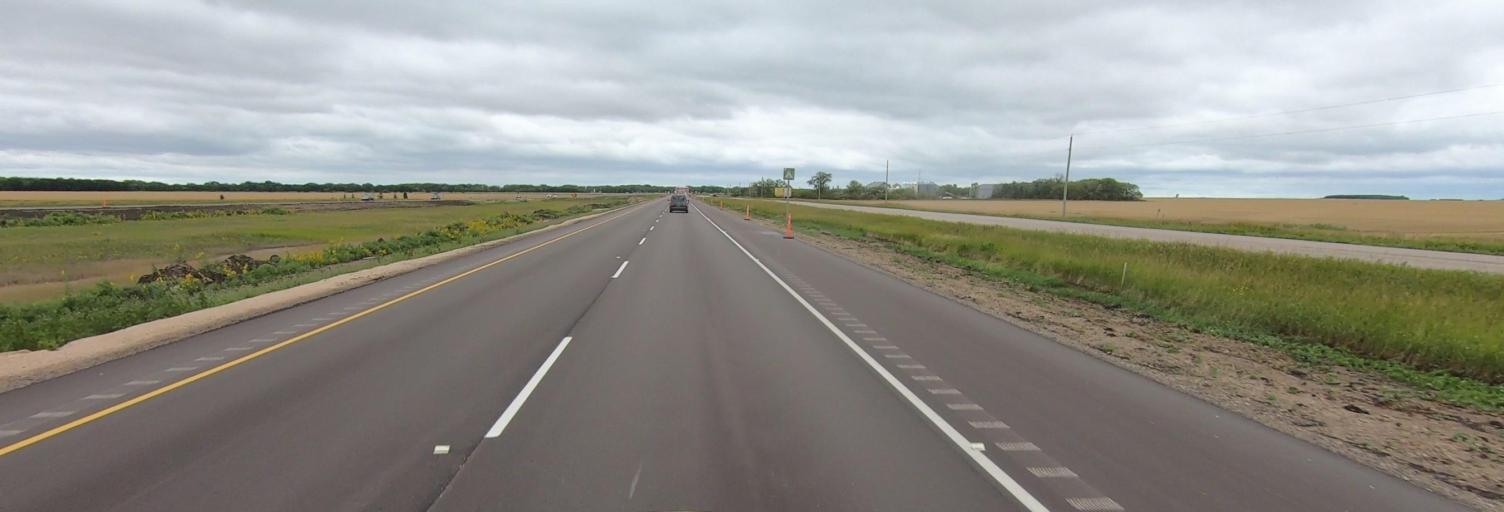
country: CA
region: Manitoba
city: Headingley
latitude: 49.8835
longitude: -97.4798
